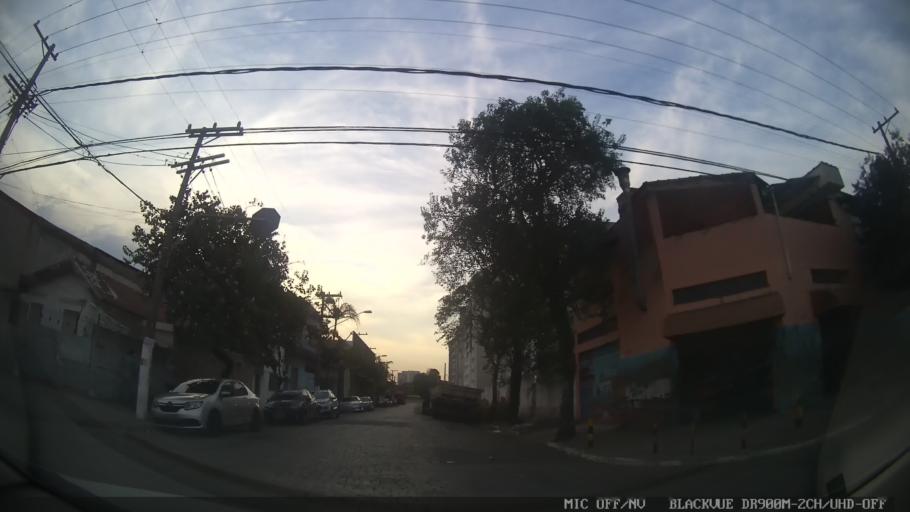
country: BR
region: Sao Paulo
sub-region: Sao Caetano Do Sul
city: Sao Caetano do Sul
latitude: -23.5990
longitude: -46.5931
